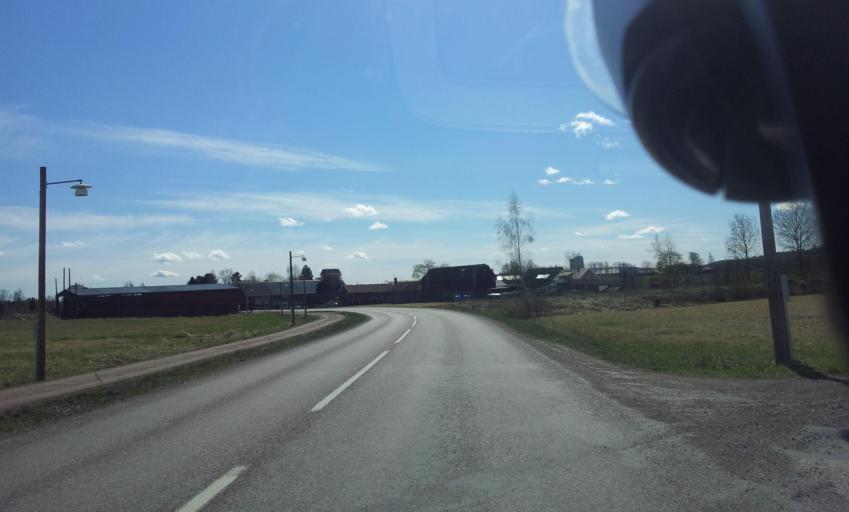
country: SE
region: Dalarna
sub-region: Borlange Kommun
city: Ornas
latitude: 60.4671
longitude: 15.5143
